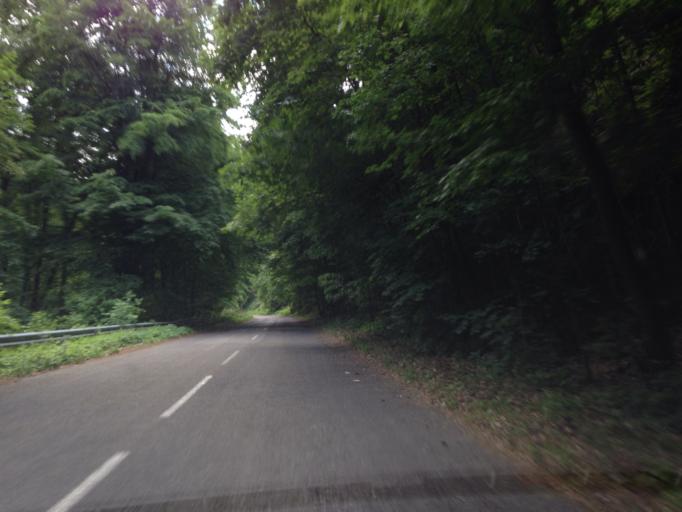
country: HU
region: Pest
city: Visegrad
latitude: 47.7439
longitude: 18.9432
